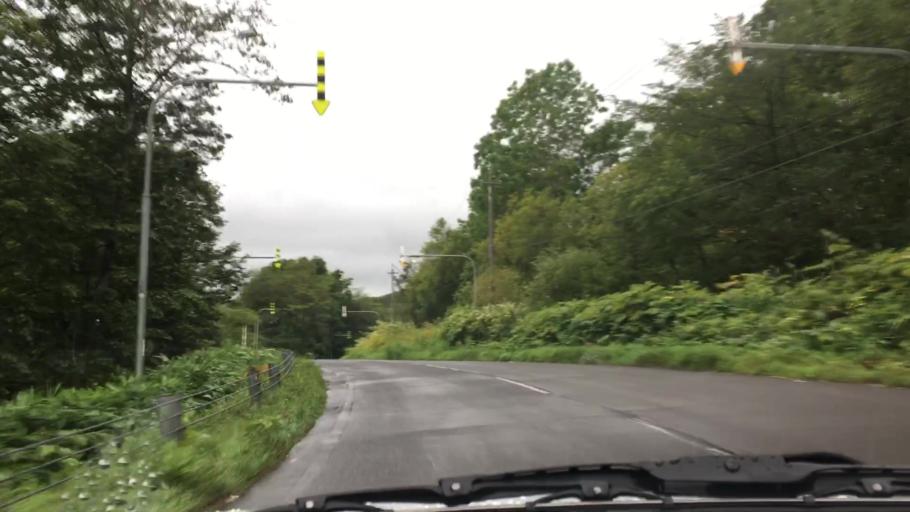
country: JP
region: Hokkaido
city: Niseko Town
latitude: 42.6618
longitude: 140.7692
